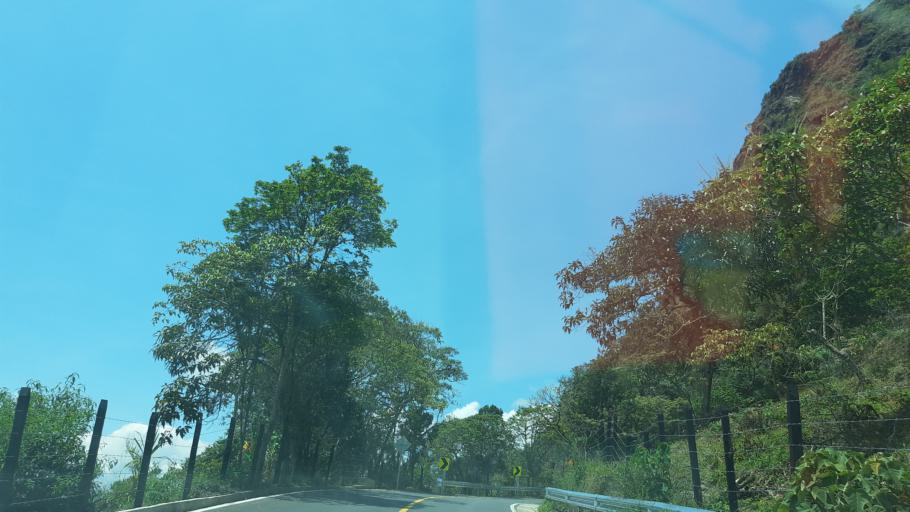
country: CO
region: Boyaca
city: Chinavita
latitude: 5.1311
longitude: -73.3880
